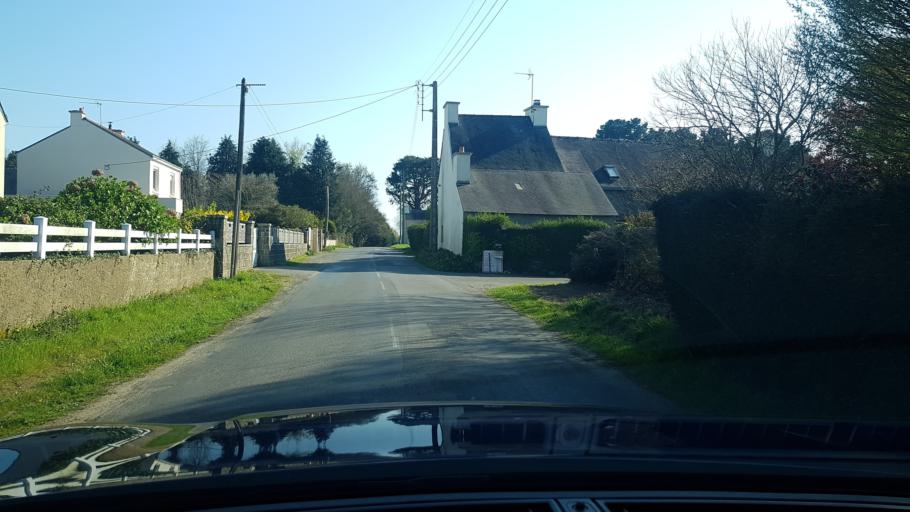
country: FR
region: Brittany
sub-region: Departement du Finistere
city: Moelan-sur-Mer
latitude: 47.7942
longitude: -3.6244
